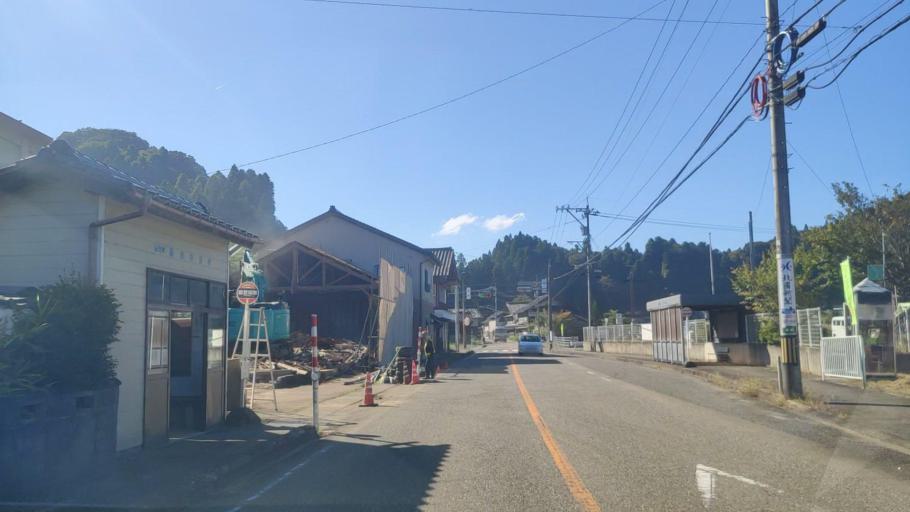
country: JP
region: Ishikawa
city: Nanao
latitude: 37.2816
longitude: 137.0413
